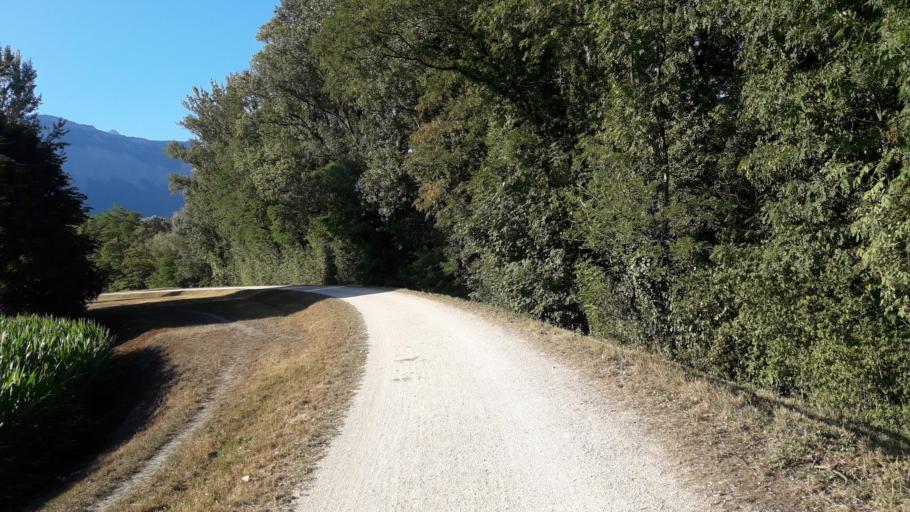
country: FR
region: Rhone-Alpes
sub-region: Departement de l'Isere
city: Gieres
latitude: 45.1995
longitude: 5.7981
